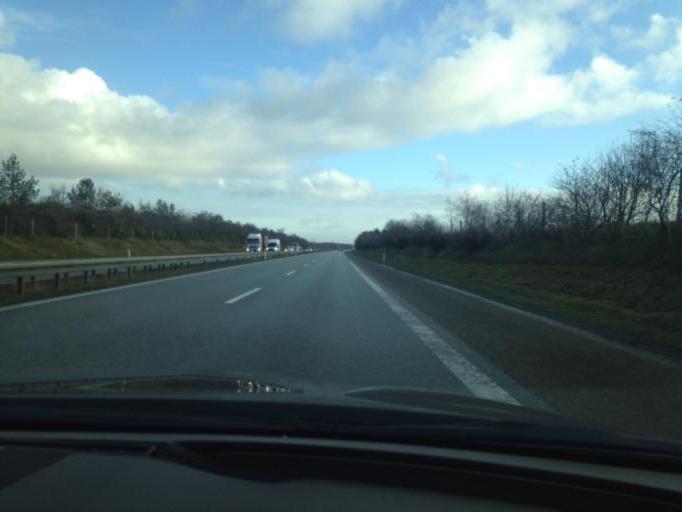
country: DK
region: South Denmark
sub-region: Vejen Kommune
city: Vejen
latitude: 55.4950
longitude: 9.1135
